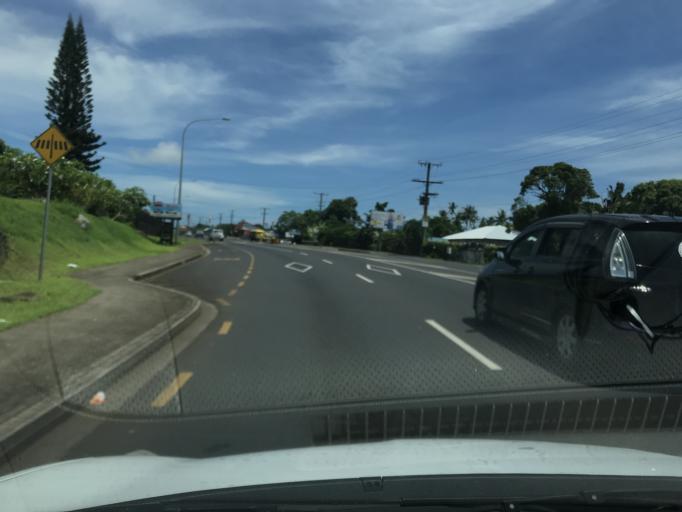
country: WS
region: Tuamasaga
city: Vaiusu
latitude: -13.8268
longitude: -171.7936
